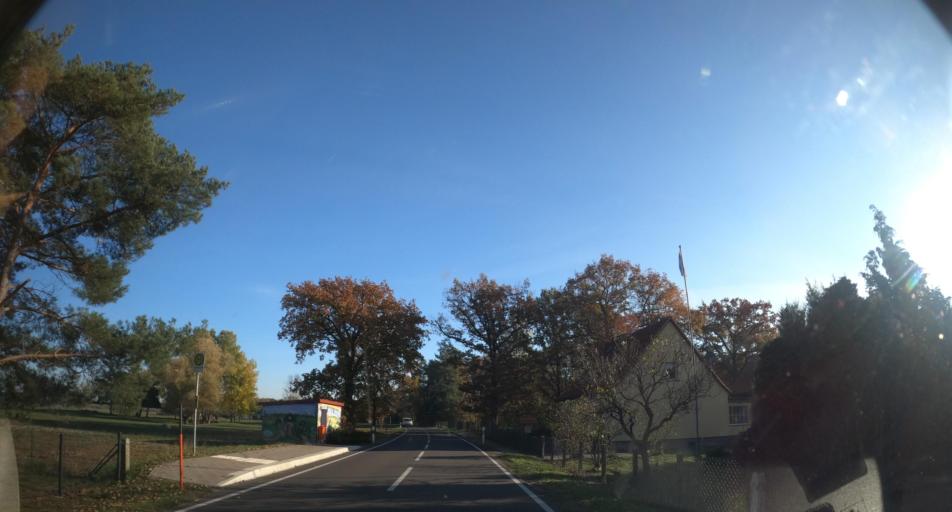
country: DE
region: Mecklenburg-Vorpommern
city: Ahlbeck
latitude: 53.6449
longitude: 14.1980
